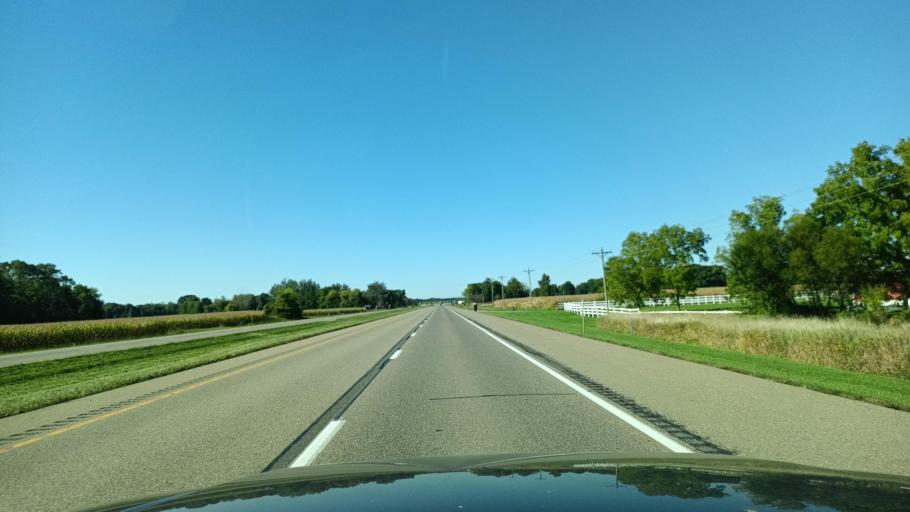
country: US
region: Iowa
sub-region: Lee County
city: Fort Madison
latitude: 40.6793
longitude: -91.2545
